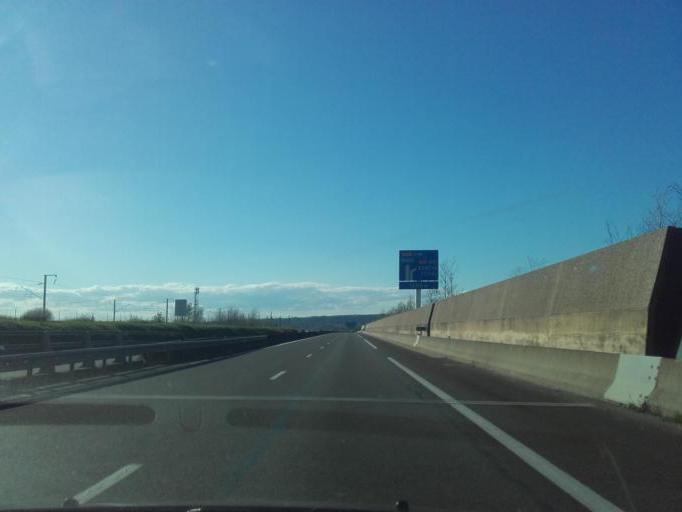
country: FR
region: Rhone-Alpes
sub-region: Departement du Rhone
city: Jonage
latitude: 45.8165
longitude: 5.0506
